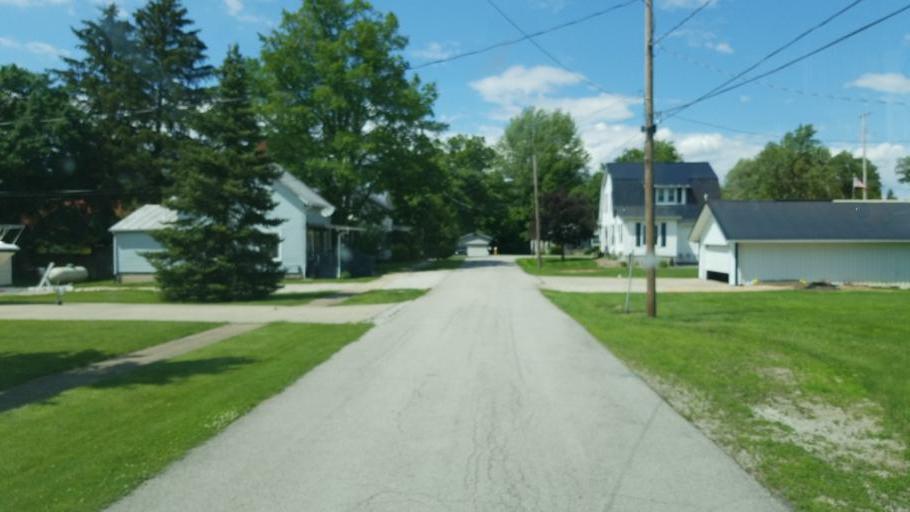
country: US
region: Ohio
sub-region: Huron County
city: Plymouth
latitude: 41.1048
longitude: -82.6141
